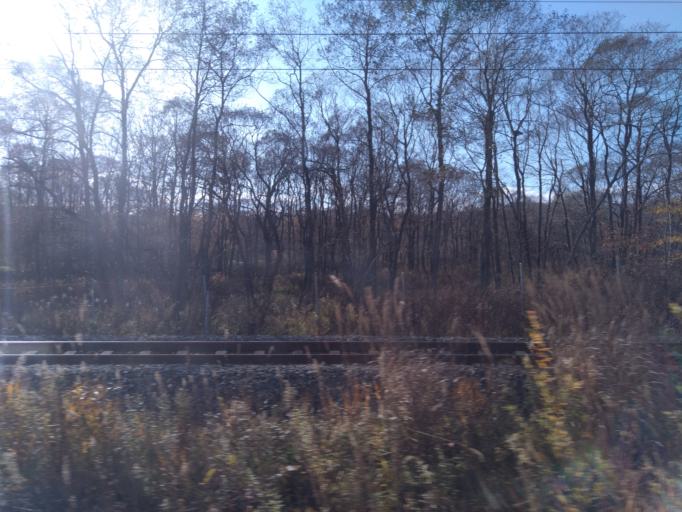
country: JP
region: Hokkaido
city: Chitose
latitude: 42.7646
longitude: 141.7215
